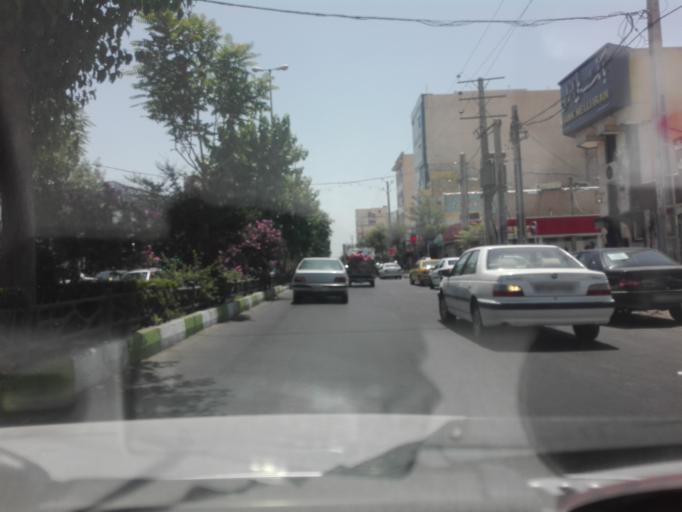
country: IR
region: Tehran
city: Shahre Jadide Andisheh
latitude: 35.7178
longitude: 50.9865
